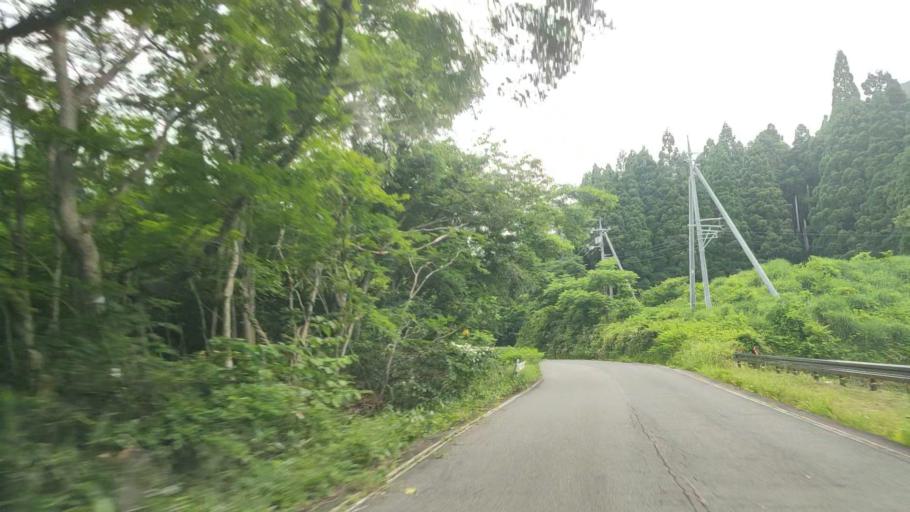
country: JP
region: Tottori
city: Yonago
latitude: 35.3279
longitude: 133.5571
